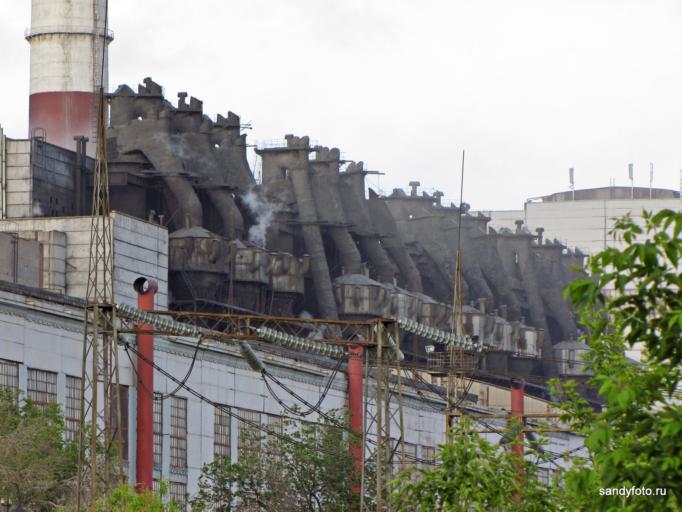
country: RU
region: Chelyabinsk
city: Troitsk
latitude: 54.0366
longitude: 61.6394
